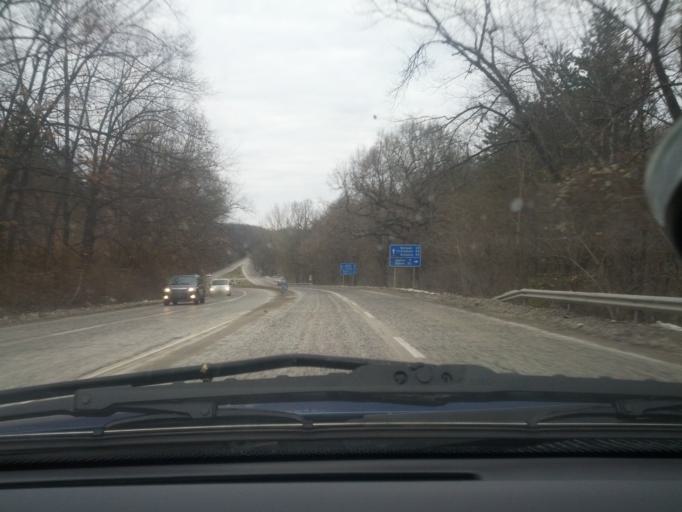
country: BG
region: Vratsa
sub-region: Obshtina Vratsa
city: Vratsa
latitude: 43.2673
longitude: 23.6066
